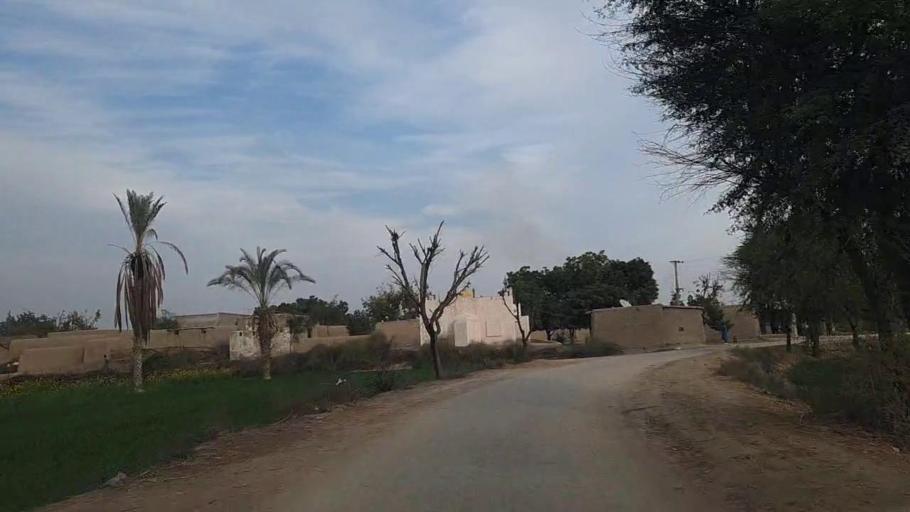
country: PK
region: Sindh
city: Daur
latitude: 26.5289
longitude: 68.4228
